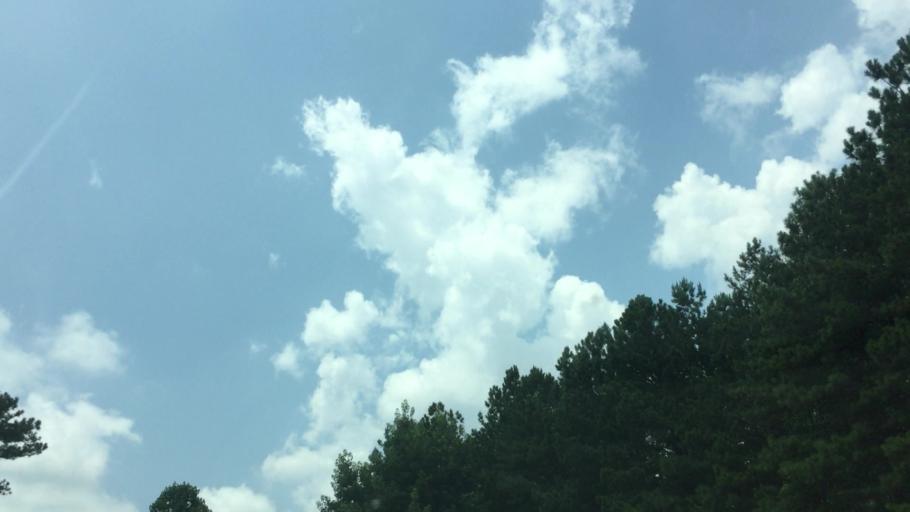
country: US
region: Georgia
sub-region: Carroll County
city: Villa Rica
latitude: 33.6154
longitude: -84.9390
